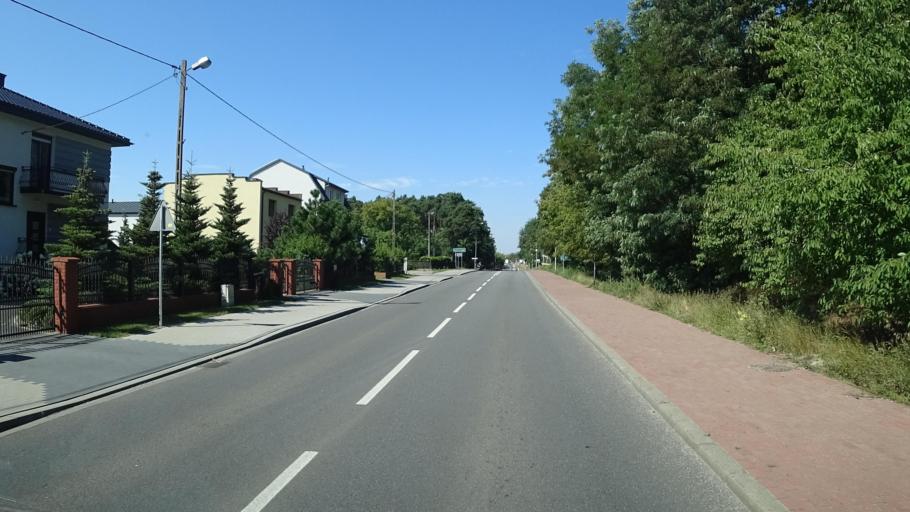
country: PL
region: Greater Poland Voivodeship
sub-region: Powiat koninski
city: Slesin
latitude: 52.3718
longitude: 18.3189
